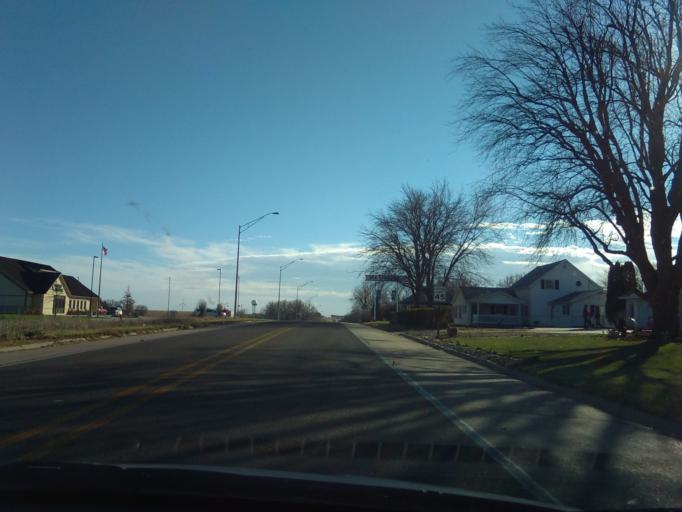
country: US
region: Nebraska
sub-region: Webster County
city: Red Cloud
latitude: 40.3334
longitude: -98.4439
